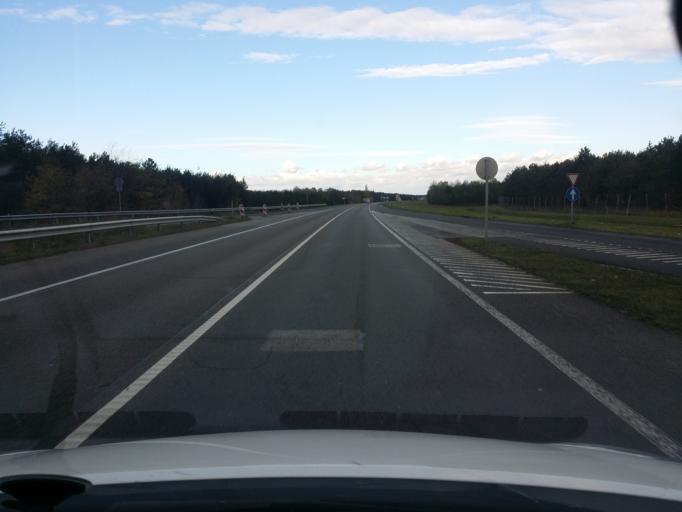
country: HU
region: Gyor-Moson-Sopron
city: Rajka
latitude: 47.9466
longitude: 17.1659
